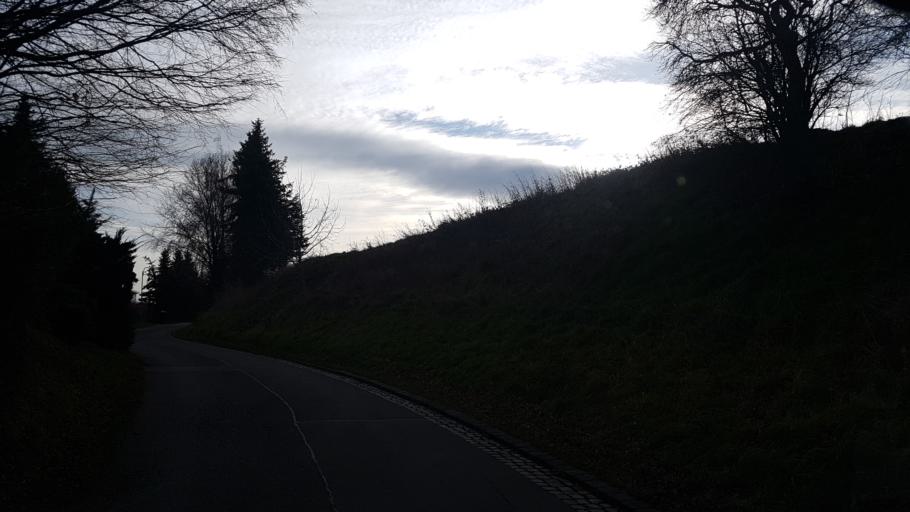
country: DE
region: Saxony
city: Ostrau
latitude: 51.1827
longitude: 13.1736
